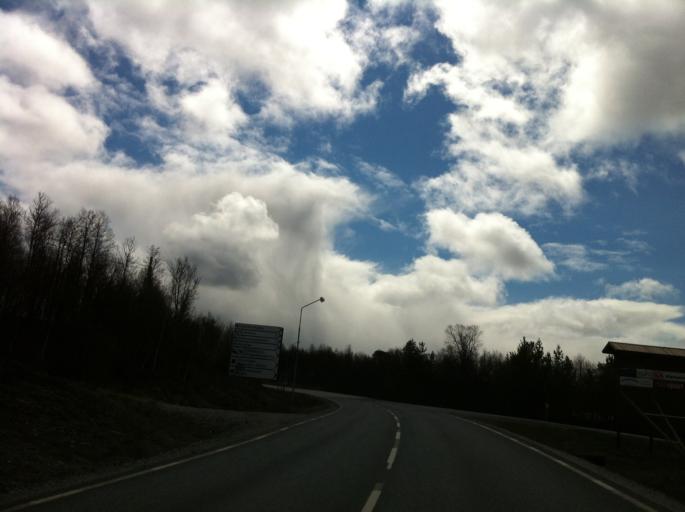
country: NO
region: Sor-Trondelag
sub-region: Tydal
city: Aas
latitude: 62.6442
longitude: 12.4278
